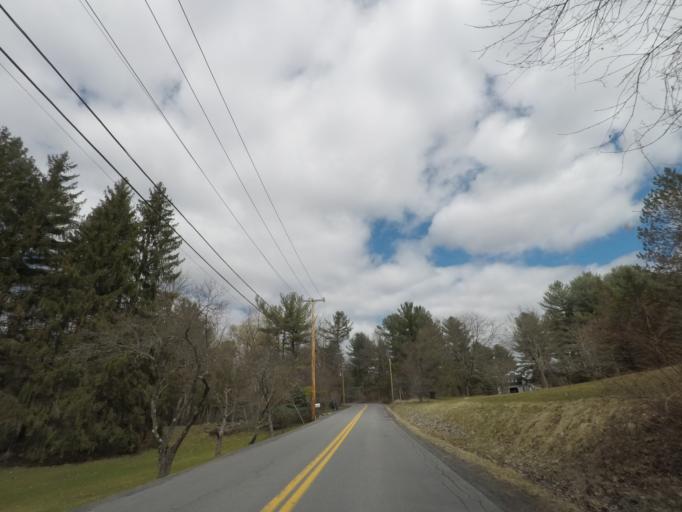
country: US
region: New York
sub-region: Albany County
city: Voorheesville
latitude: 42.6299
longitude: -73.8837
